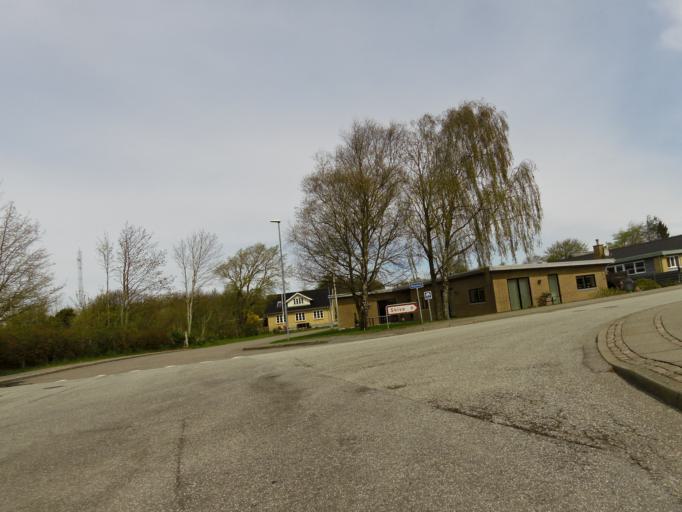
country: DK
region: Central Jutland
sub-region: Skive Kommune
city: Skive
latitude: 56.5350
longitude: 8.9328
